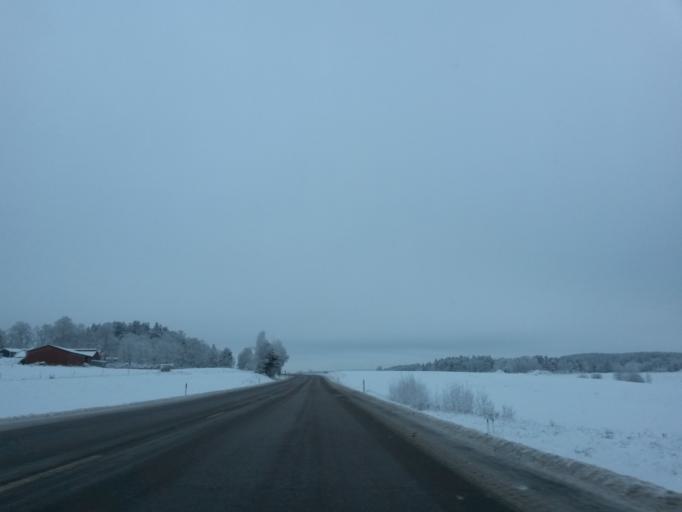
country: SE
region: Vaestra Goetaland
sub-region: Vargarda Kommun
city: Vargarda
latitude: 58.0550
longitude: 12.8175
